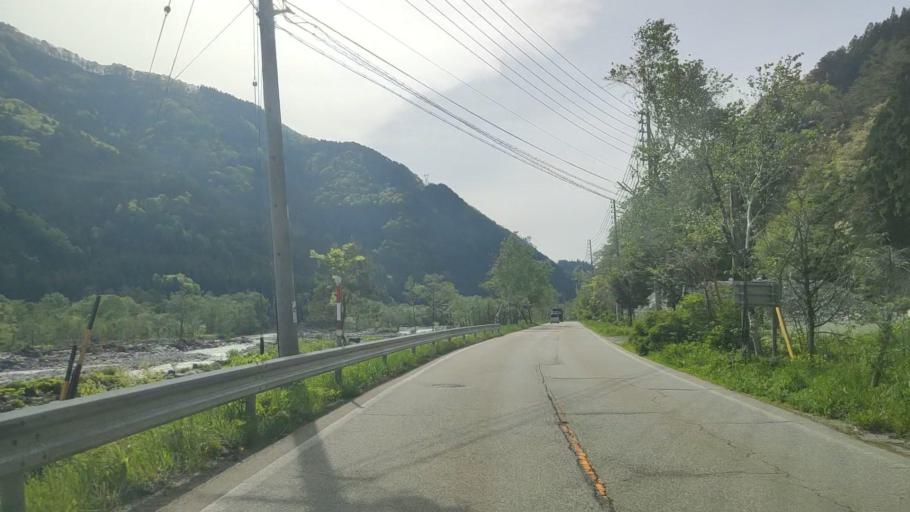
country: JP
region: Gifu
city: Takayama
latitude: 36.2493
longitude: 137.4869
